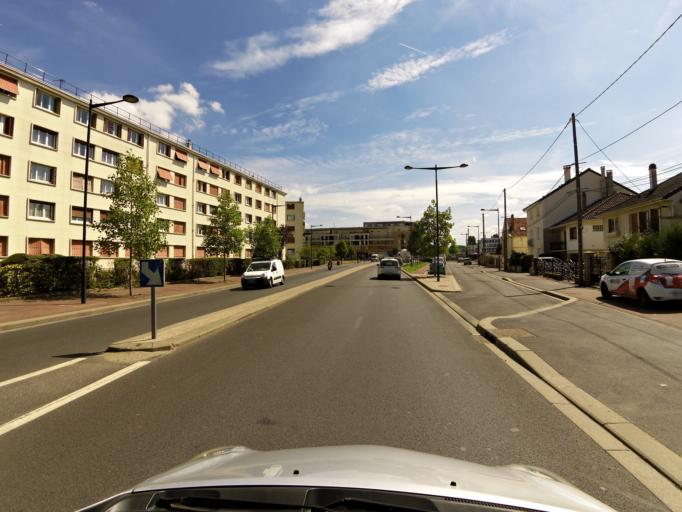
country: FR
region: Ile-de-France
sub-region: Departement de Seine-Saint-Denis
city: Gournay-sur-Marne
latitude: 48.8701
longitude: 2.5864
